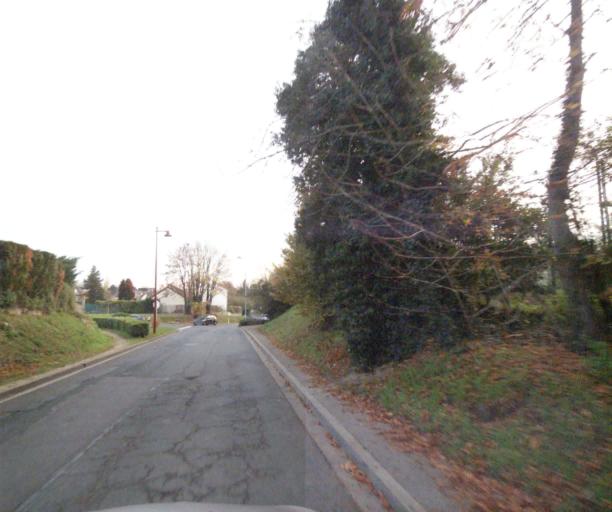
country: FR
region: Ile-de-France
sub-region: Departement des Yvelines
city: Triel-sur-Seine
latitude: 48.9775
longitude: 2.0092
